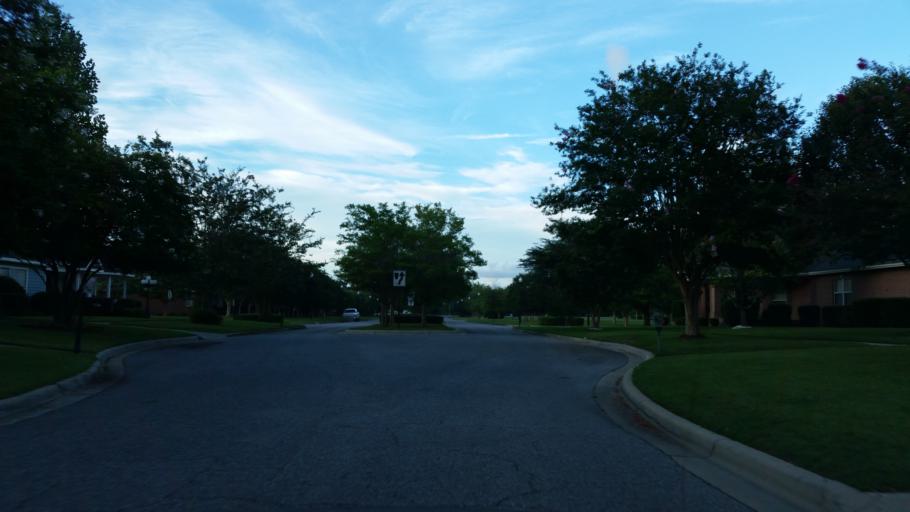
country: US
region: Florida
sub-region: Escambia County
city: Ensley
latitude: 30.5375
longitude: -87.3078
